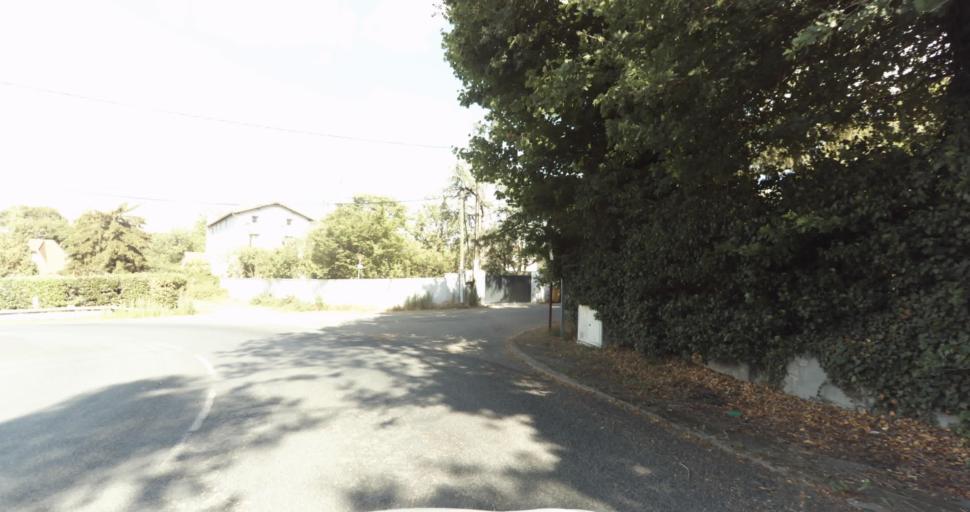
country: FR
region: Rhone-Alpes
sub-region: Departement du Rhone
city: Francheville
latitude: 45.7221
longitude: 4.7673
